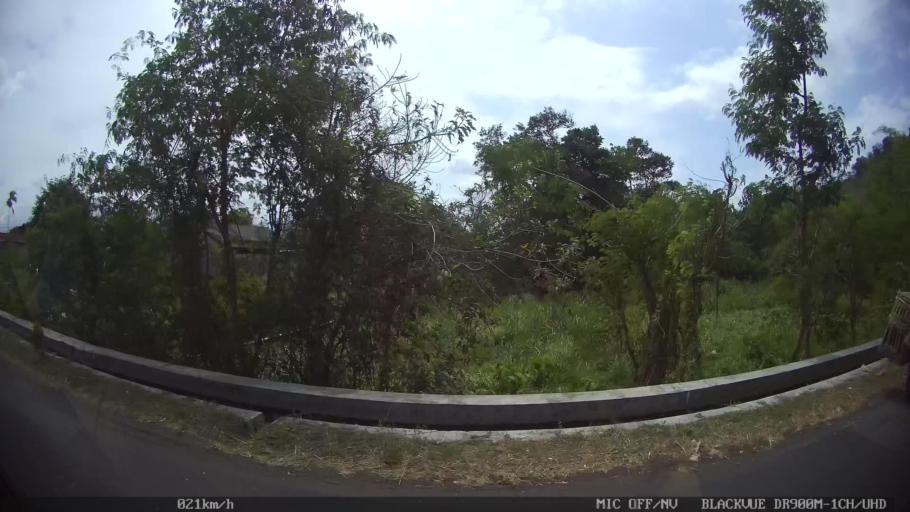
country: ID
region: Central Java
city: Candi Prambanan
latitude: -7.7727
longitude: 110.4804
